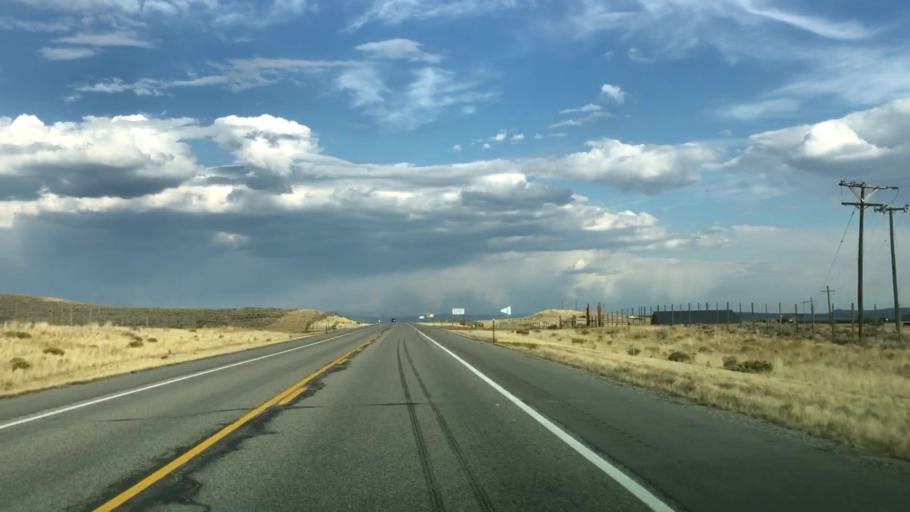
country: US
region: Wyoming
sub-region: Sublette County
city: Pinedale
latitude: 42.8894
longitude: -110.0586
